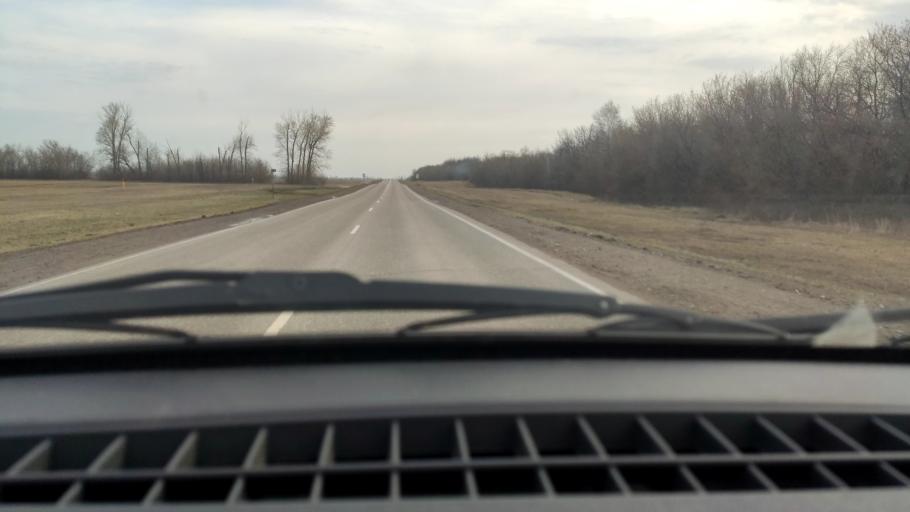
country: RU
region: Bashkortostan
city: Davlekanovo
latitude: 54.2658
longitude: 55.0946
